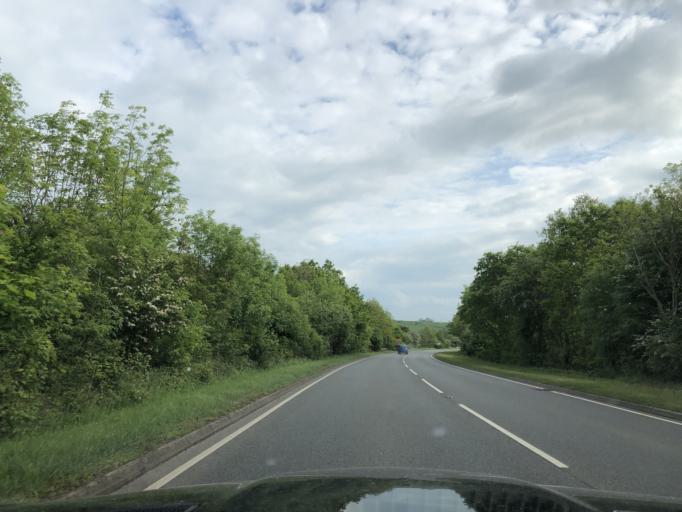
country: GB
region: England
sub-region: Warwickshire
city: Wellesbourne Mountford
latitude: 52.1340
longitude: -1.6140
